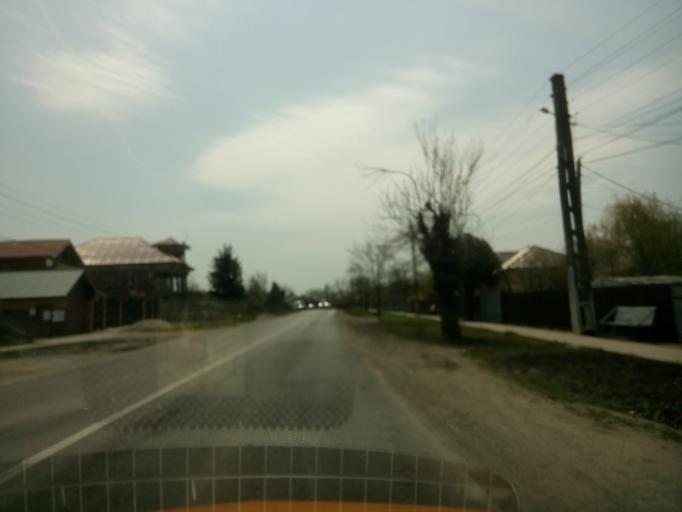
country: RO
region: Calarasi
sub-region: Comuna Soldanu
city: Negoesti
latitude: 44.2309
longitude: 26.5040
